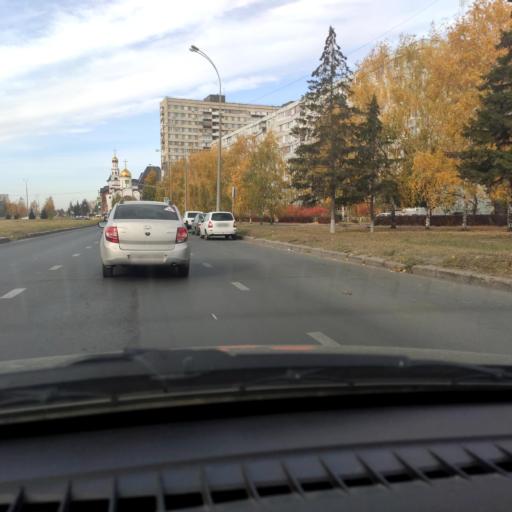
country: RU
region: Samara
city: Tol'yatti
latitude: 53.5287
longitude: 49.2863
